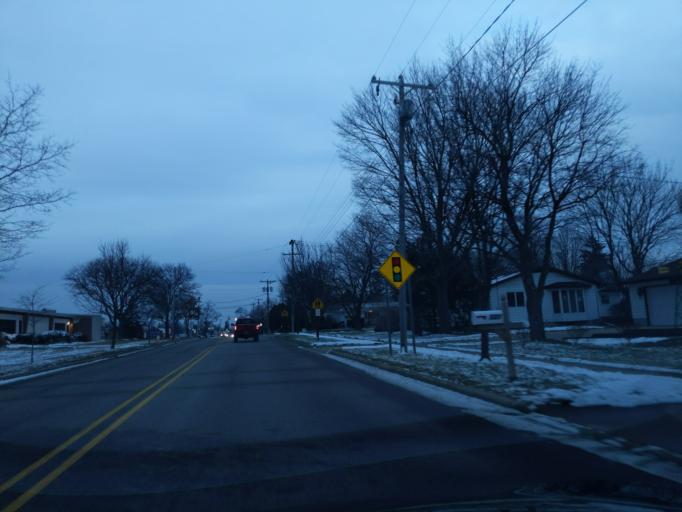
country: US
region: Michigan
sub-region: Ingham County
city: Mason
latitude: 42.5775
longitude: -84.4529
